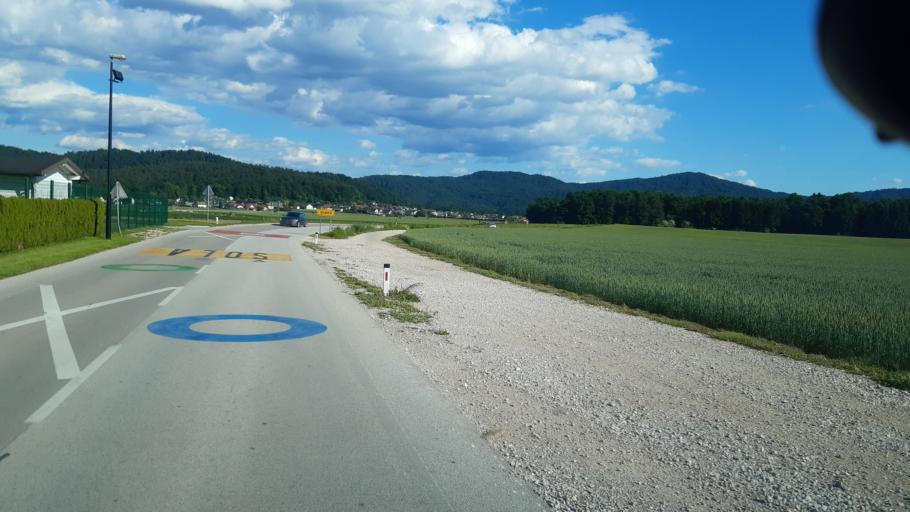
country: SI
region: Vodice
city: Vodice
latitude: 46.1846
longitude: 14.4960
